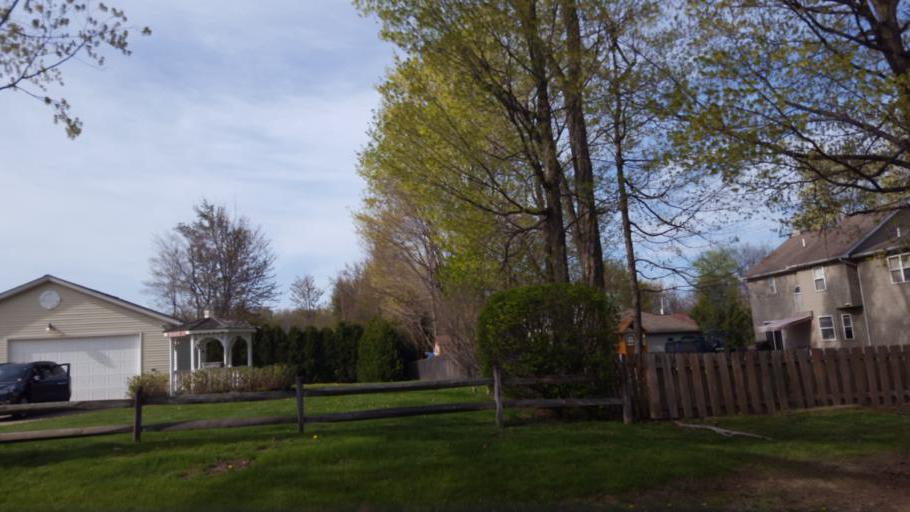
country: US
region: Ohio
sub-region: Lake County
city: North Madison
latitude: 41.8419
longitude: -81.0095
